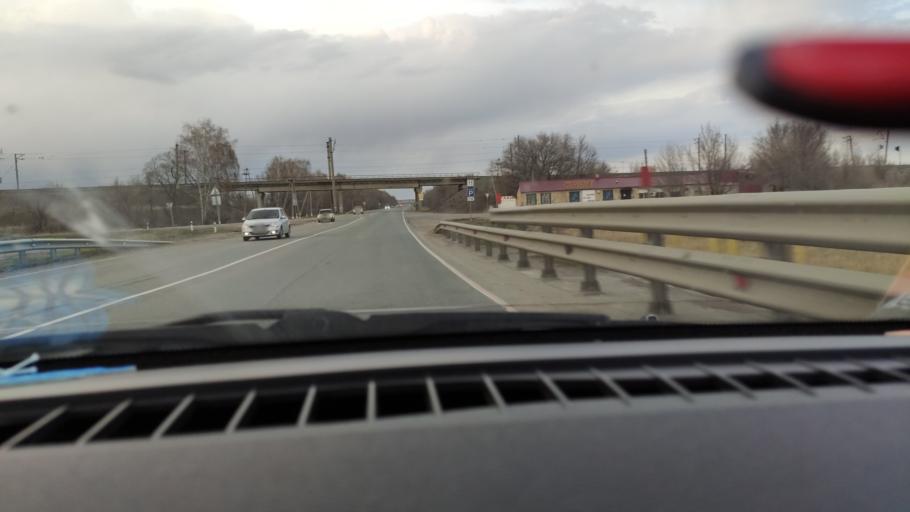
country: RU
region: Saratov
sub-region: Saratovskiy Rayon
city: Saratov
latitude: 51.6997
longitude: 46.0105
